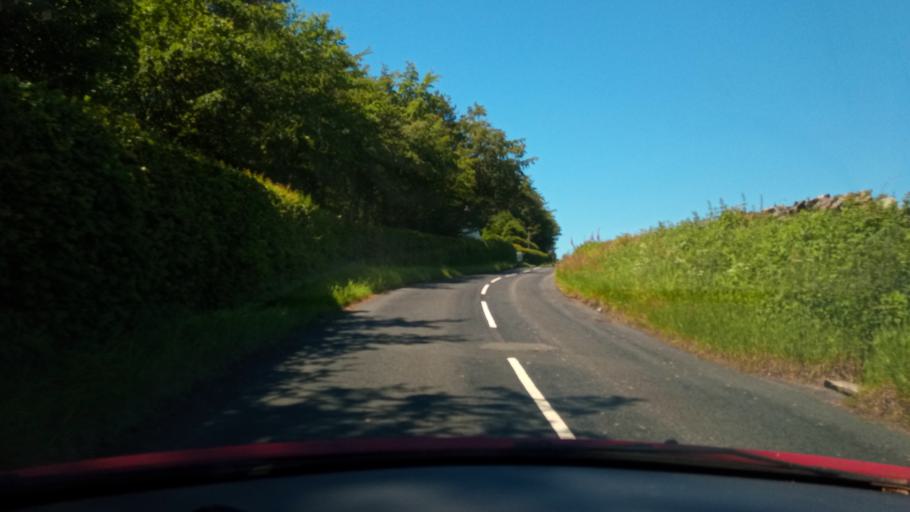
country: GB
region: Scotland
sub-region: The Scottish Borders
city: Duns
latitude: 55.7773
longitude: -2.4074
